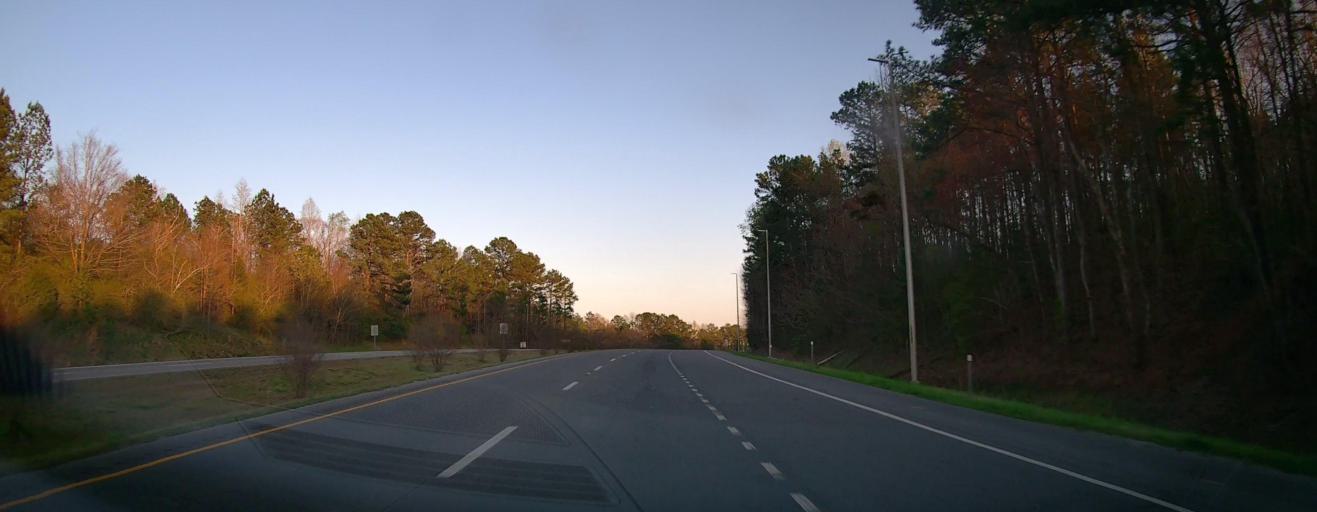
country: US
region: Alabama
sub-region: Talladega County
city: Sylacauga
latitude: 33.1413
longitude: -86.2528
